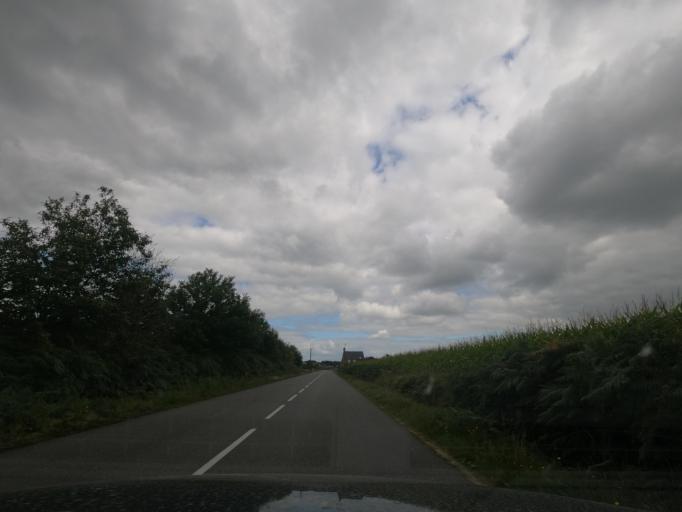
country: FR
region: Brittany
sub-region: Departement d'Ille-et-Vilaine
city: Landean
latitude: 48.4273
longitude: -1.1208
